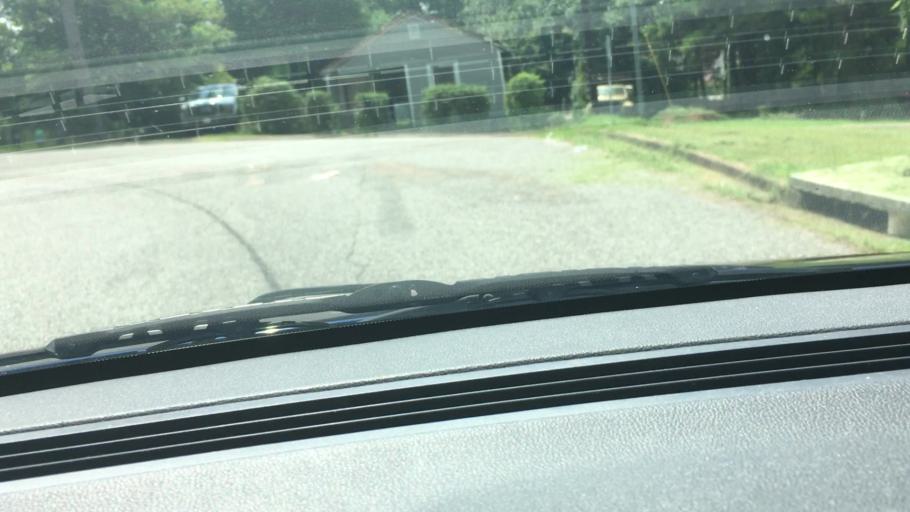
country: US
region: Alabama
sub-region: Tuscaloosa County
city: Northport
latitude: 33.2426
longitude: -87.5846
